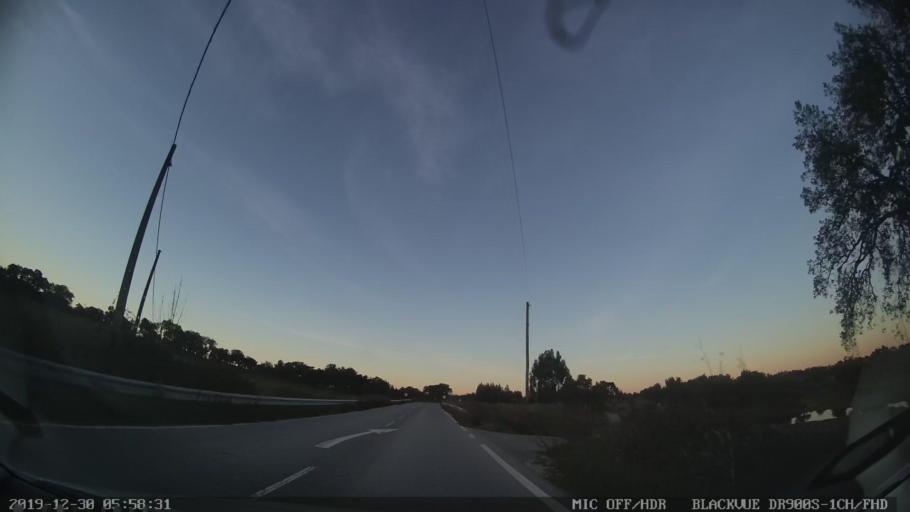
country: PT
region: Castelo Branco
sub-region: Idanha-A-Nova
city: Idanha-a-Nova
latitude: 40.0354
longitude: -7.2423
